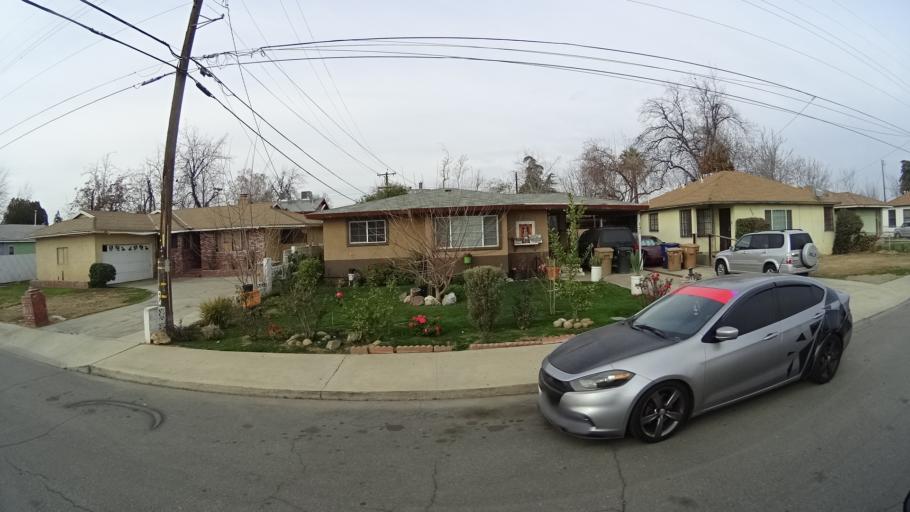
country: US
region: California
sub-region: Kern County
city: Bakersfield
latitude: 35.3561
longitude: -119.0130
